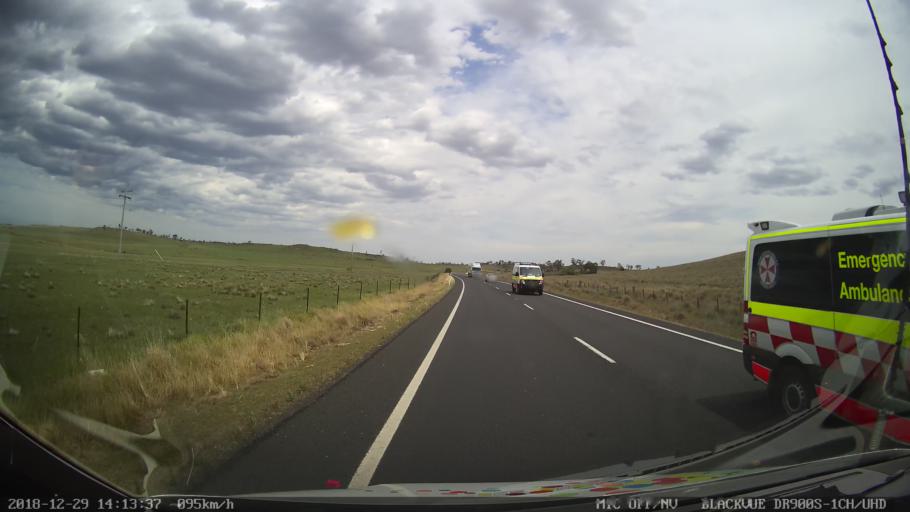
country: AU
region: New South Wales
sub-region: Cooma-Monaro
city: Cooma
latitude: -36.4306
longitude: 149.2384
